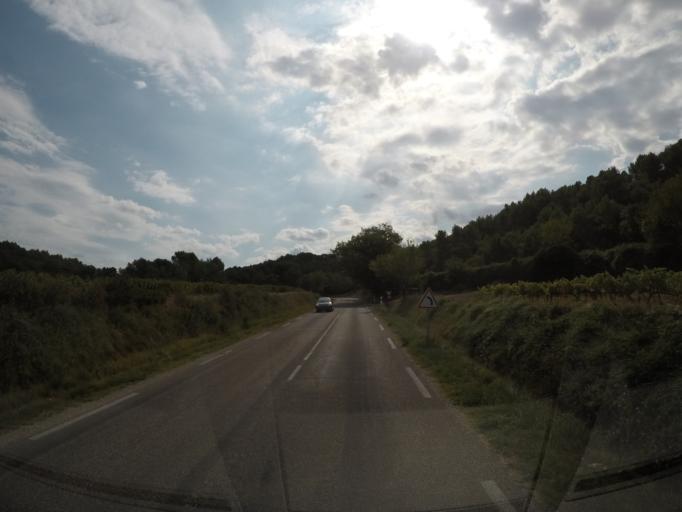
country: FR
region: Provence-Alpes-Cote d'Azur
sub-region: Departement du Vaucluse
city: Ansouis
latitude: 43.7288
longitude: 5.4898
